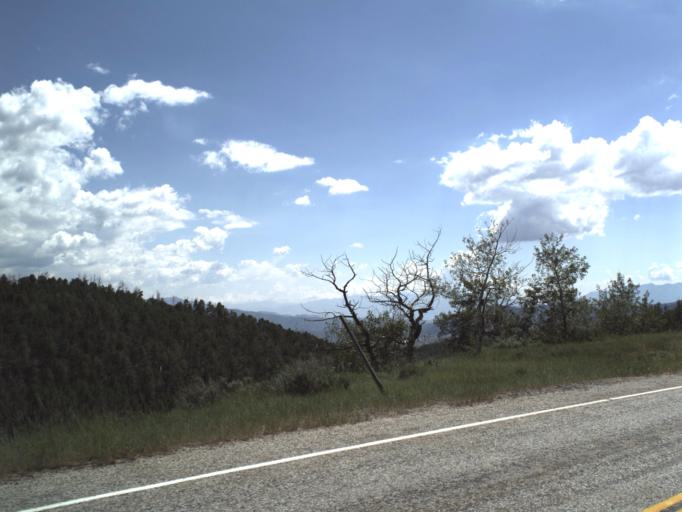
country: US
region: Utah
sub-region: Weber County
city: Wolf Creek
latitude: 41.4060
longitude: -111.5485
